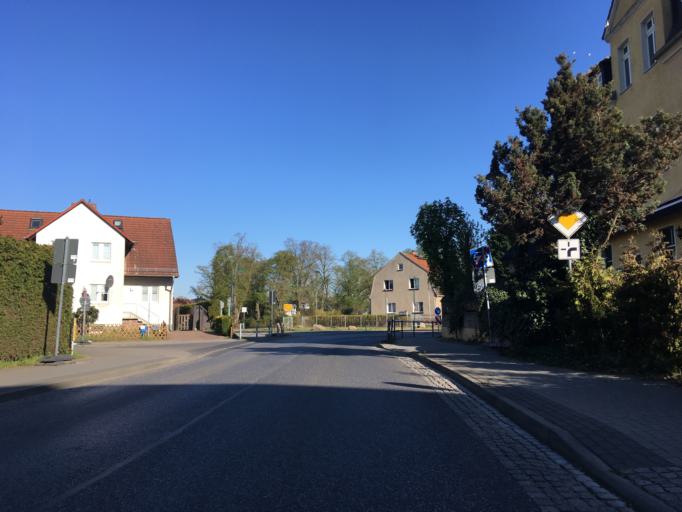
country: DE
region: Berlin
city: Buch
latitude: 52.6670
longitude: 13.5280
